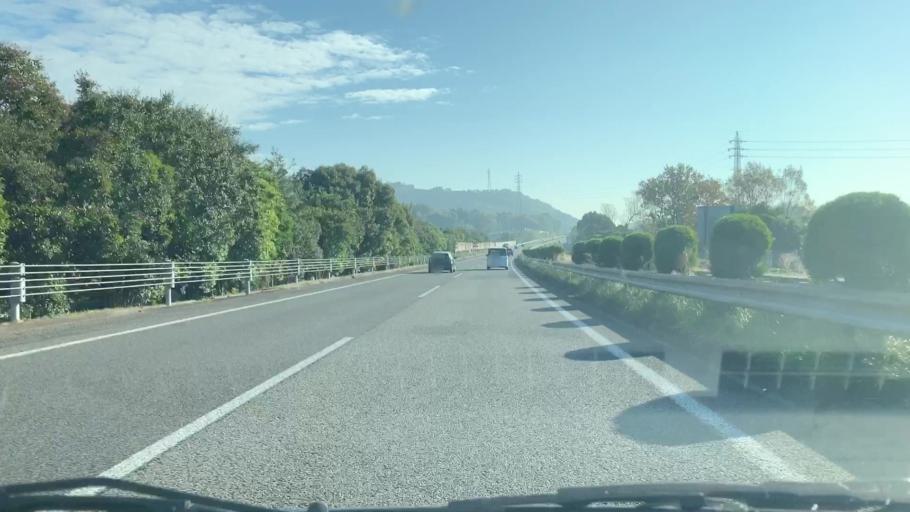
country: JP
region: Saga Prefecture
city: Takeocho-takeo
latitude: 33.2885
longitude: 130.1383
